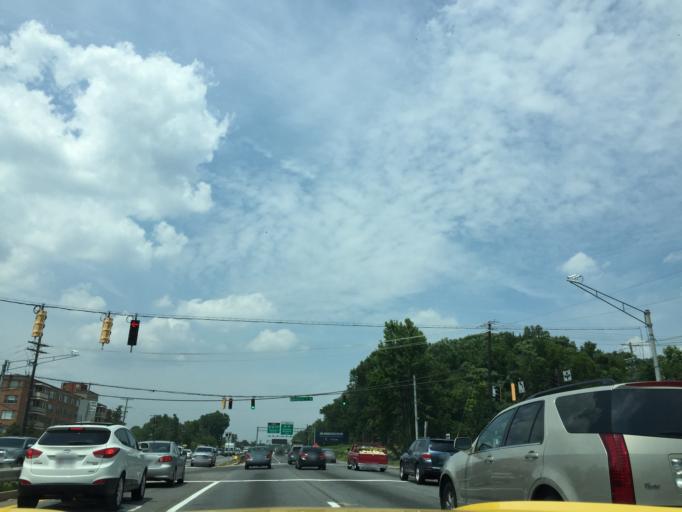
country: US
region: Maryland
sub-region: Prince George's County
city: Oxon Hill
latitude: 38.7799
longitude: -76.9972
